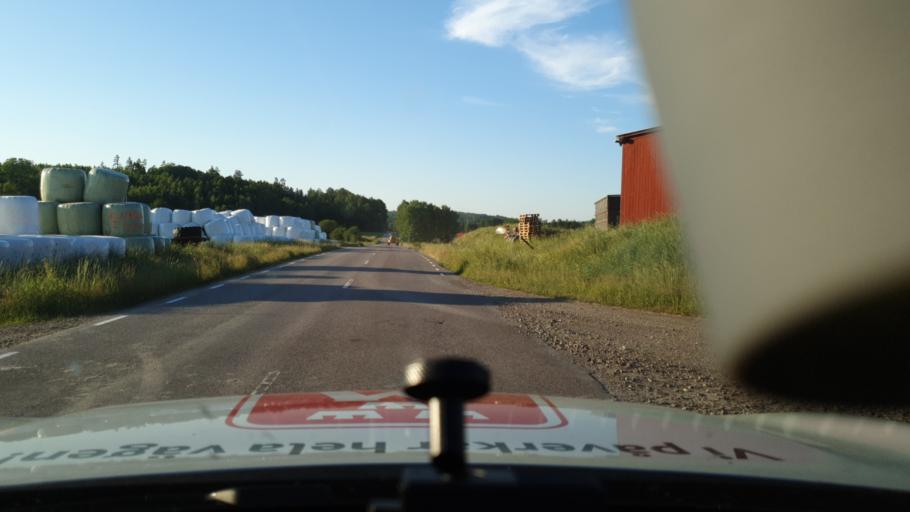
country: SE
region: Vaermland
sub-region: Kils Kommun
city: Kil
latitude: 59.5599
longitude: 13.2889
